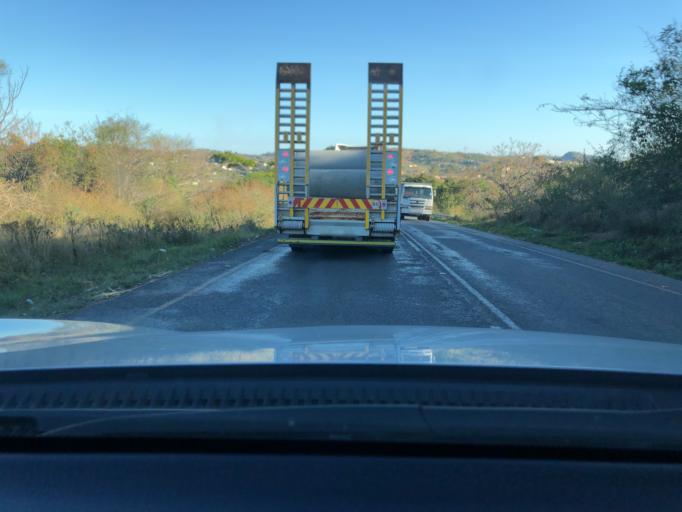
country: ZA
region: KwaZulu-Natal
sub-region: eThekwini Metropolitan Municipality
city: Umkomaas
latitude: -30.0329
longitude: 30.8104
